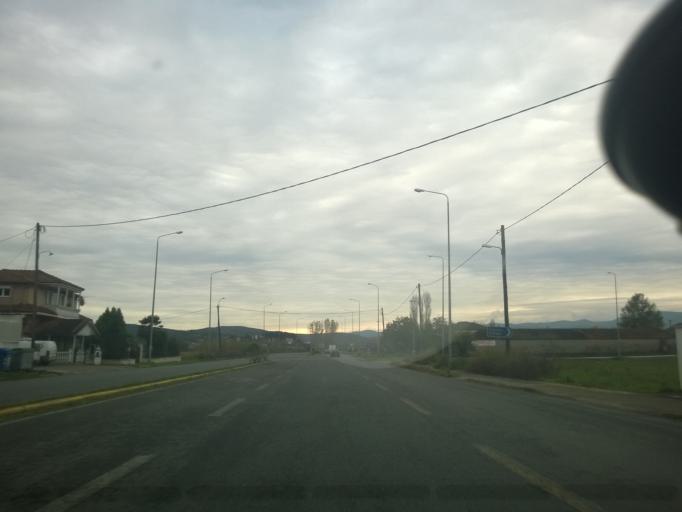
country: GR
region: Central Macedonia
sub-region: Nomos Pellis
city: Aridaia
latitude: 40.9348
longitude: 22.0844
